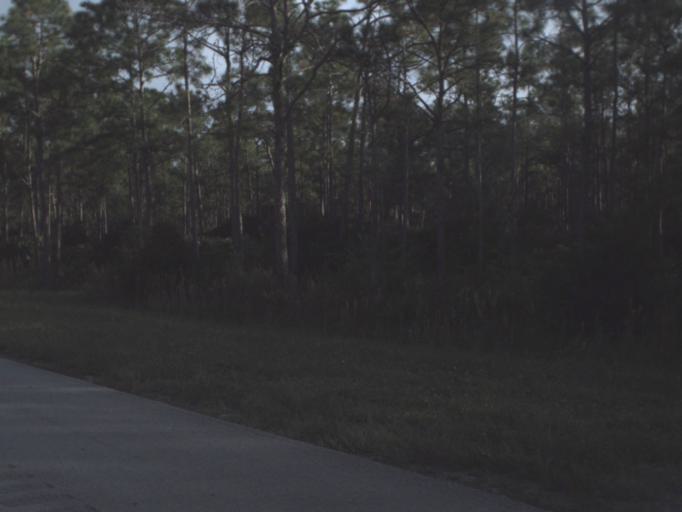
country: US
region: Florida
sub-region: Lee County
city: Gateway
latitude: 26.5815
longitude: -81.7939
